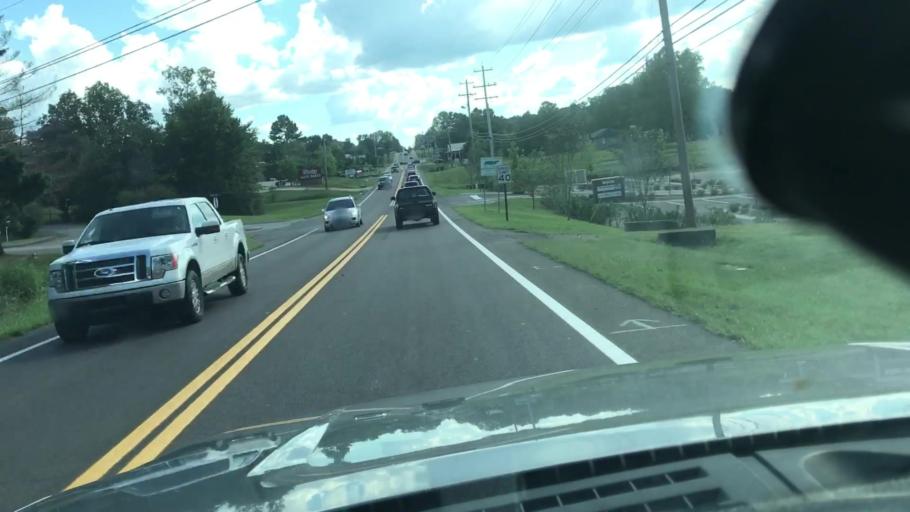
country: US
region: Tennessee
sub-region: Williamson County
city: Fairview
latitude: 35.9658
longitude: -87.1333
